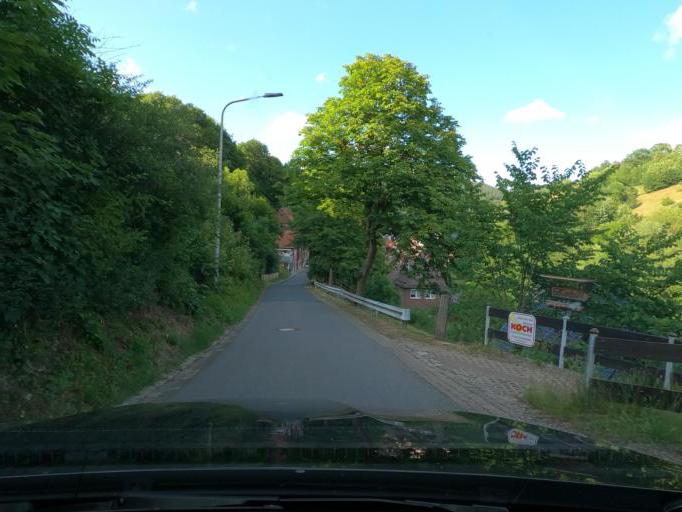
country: DE
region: Lower Saxony
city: Osterode am Harz
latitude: 51.7510
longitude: 10.2882
